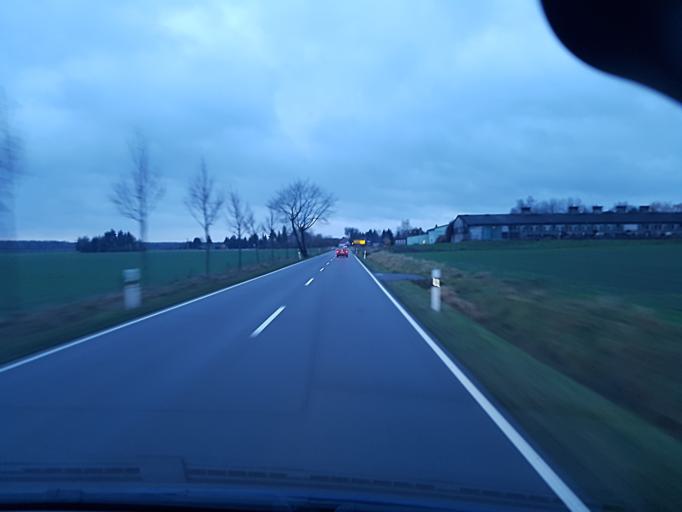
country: DE
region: Brandenburg
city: Sallgast
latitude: 51.6212
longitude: 13.8187
